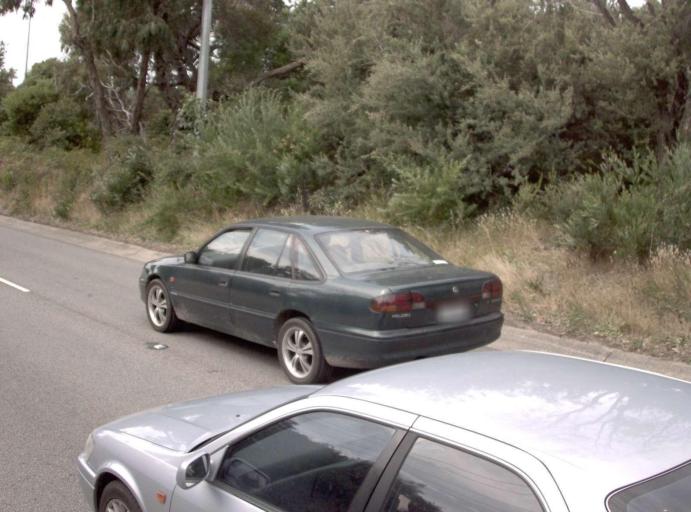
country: AU
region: Victoria
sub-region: Frankston
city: Frankston South
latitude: -38.1601
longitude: 145.1354
